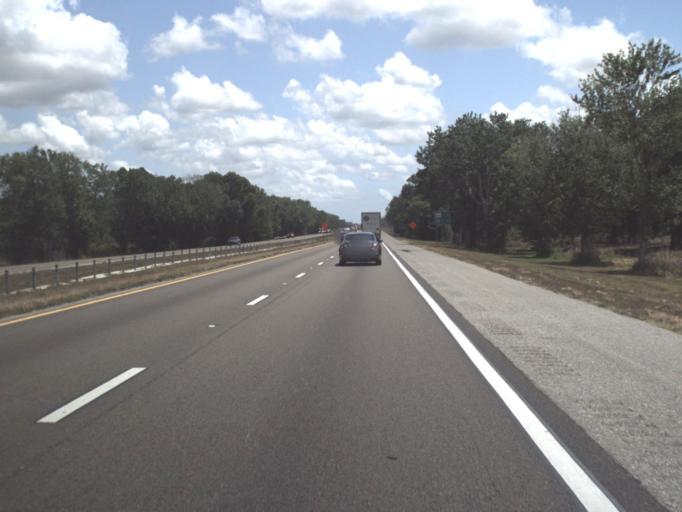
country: US
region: Florida
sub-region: Orange County
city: Wedgefield
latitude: 28.4514
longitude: -81.1250
